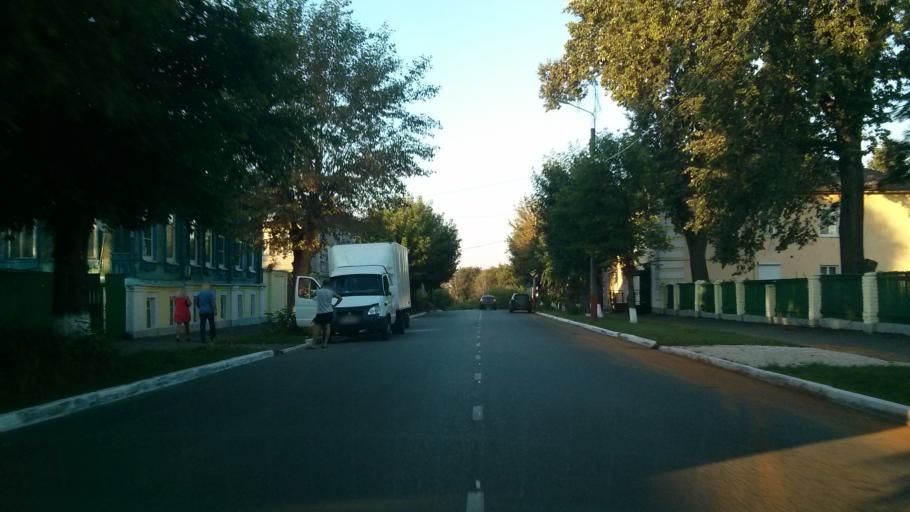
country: RU
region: Vladimir
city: Murom
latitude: 55.5771
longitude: 42.0561
